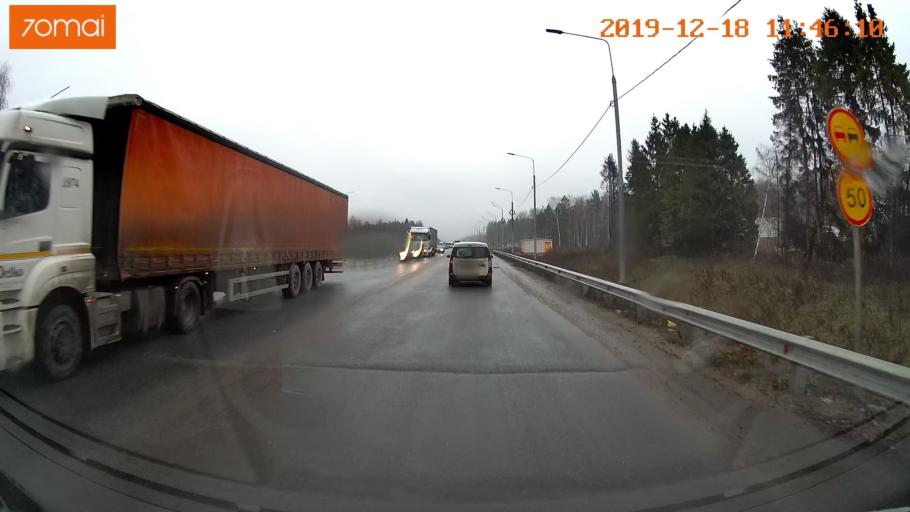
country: RU
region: Moskovskaya
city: Zvenigorod
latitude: 55.7477
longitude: 36.8861
